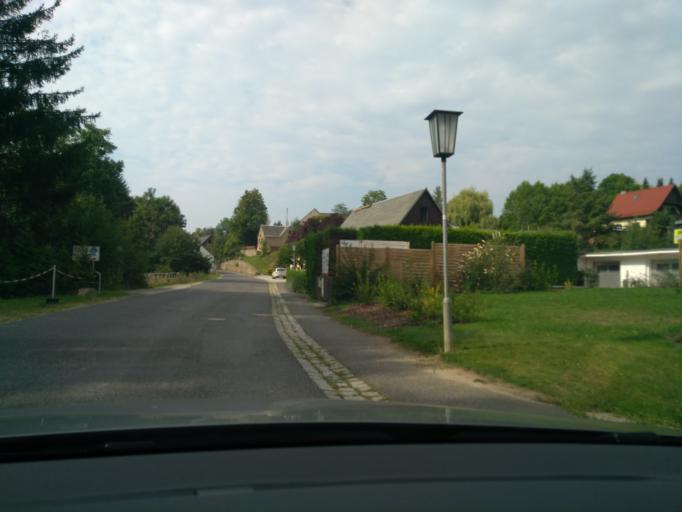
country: DE
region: Saxony
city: Markersdorf
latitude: 51.1448
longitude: 14.8805
